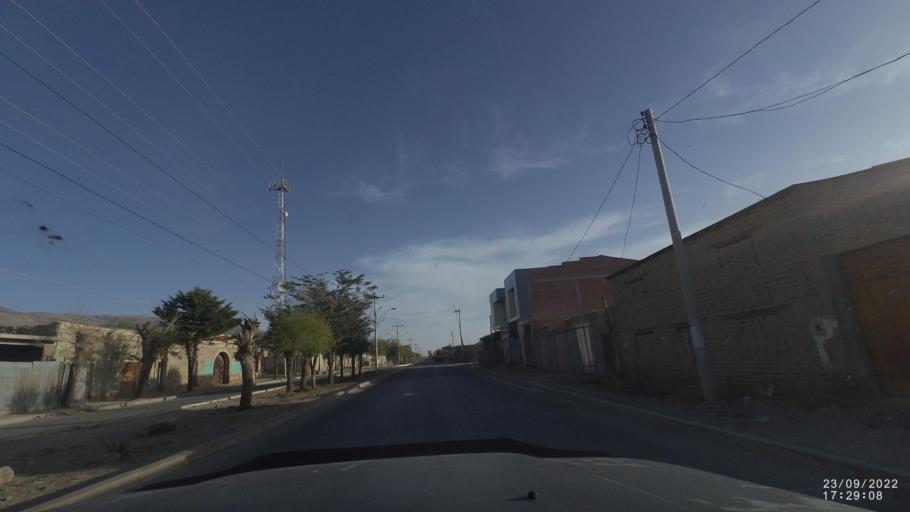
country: BO
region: Oruro
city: Challapata
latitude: -18.9004
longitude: -66.7769
